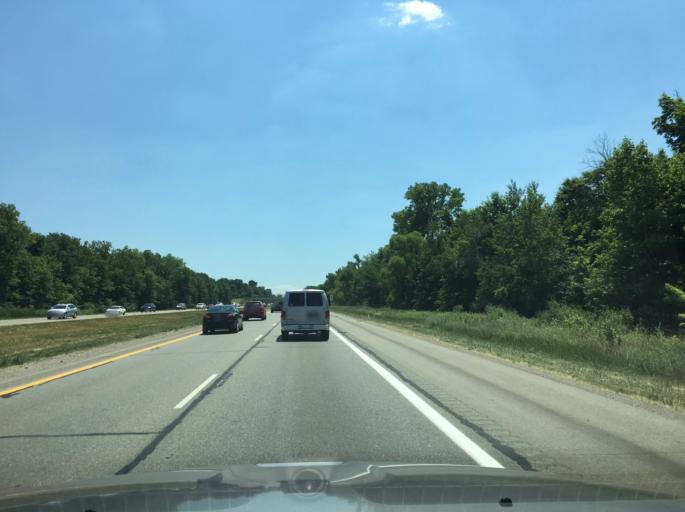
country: US
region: Michigan
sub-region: Macomb County
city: Shelby
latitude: 42.6606
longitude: -83.0146
